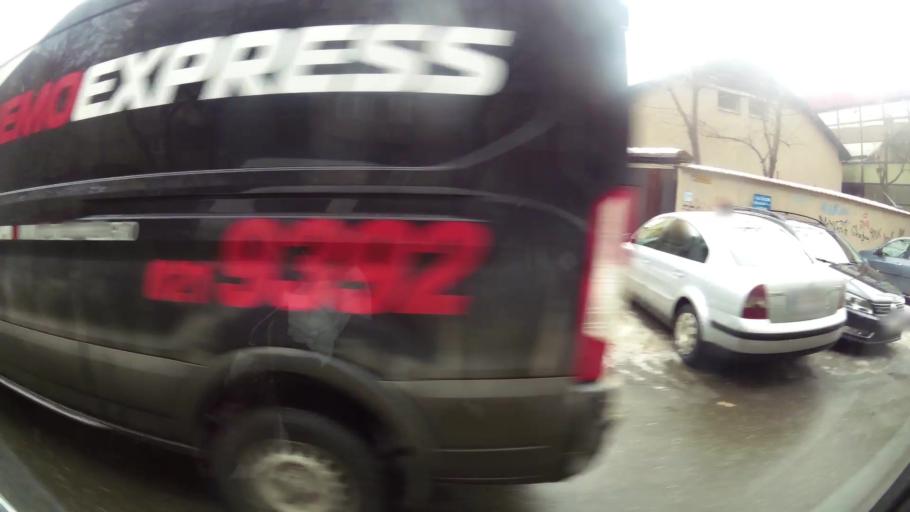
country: RO
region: Bucuresti
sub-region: Municipiul Bucuresti
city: Bucuresti
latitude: 44.4121
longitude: 26.0639
